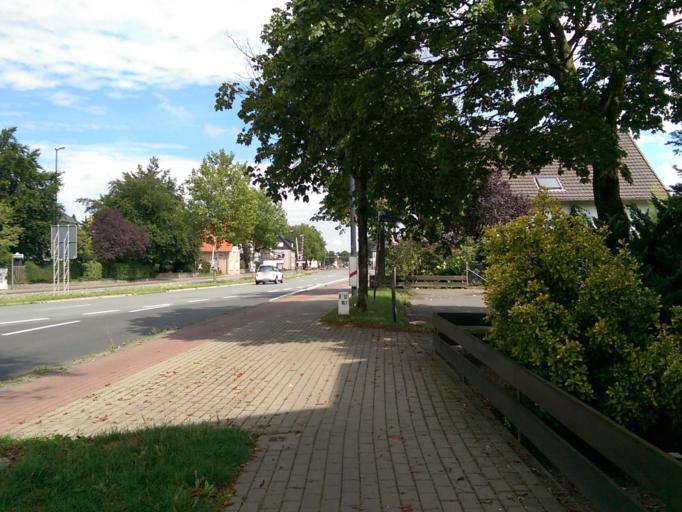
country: DE
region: North Rhine-Westphalia
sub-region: Regierungsbezirk Detmold
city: Guetersloh
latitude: 51.9159
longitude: 8.3921
